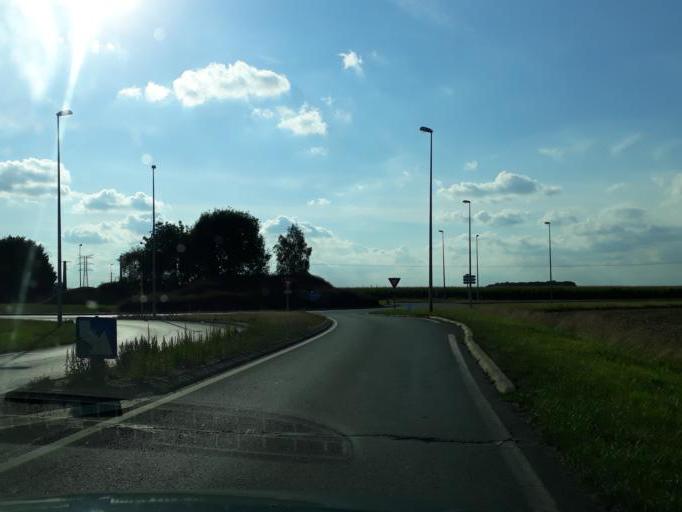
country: FR
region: Centre
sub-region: Departement du Loir-et-Cher
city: Moree
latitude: 47.9044
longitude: 1.3108
